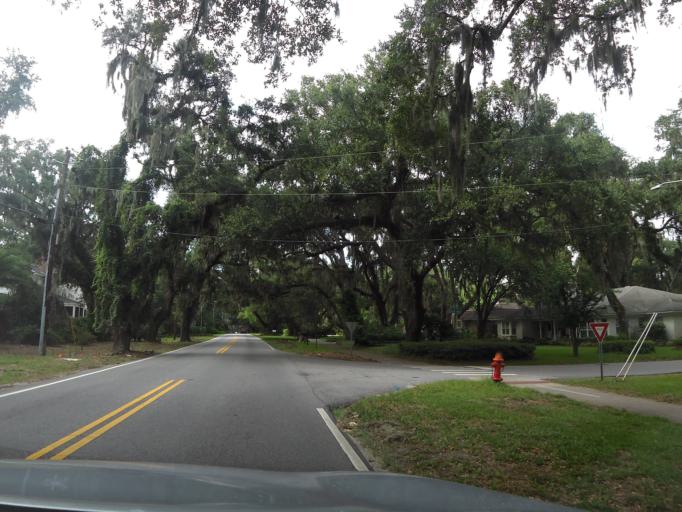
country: US
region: Georgia
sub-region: Glynn County
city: Saint Simons Island
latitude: 31.1388
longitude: -81.3971
